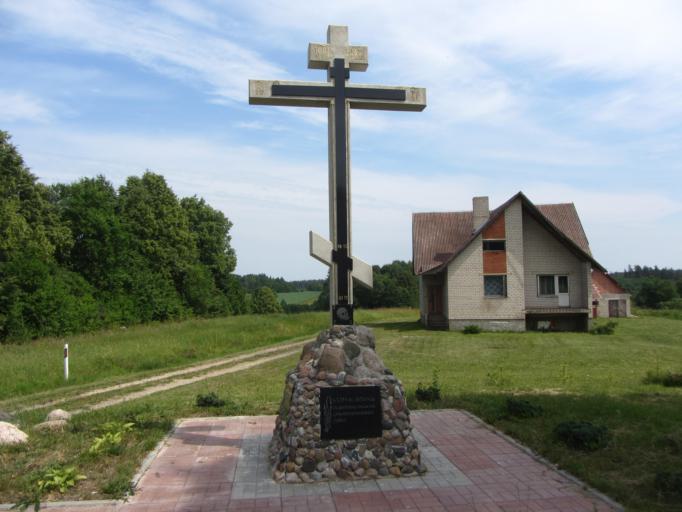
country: LT
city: Zarasai
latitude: 55.6591
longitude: 26.0712
